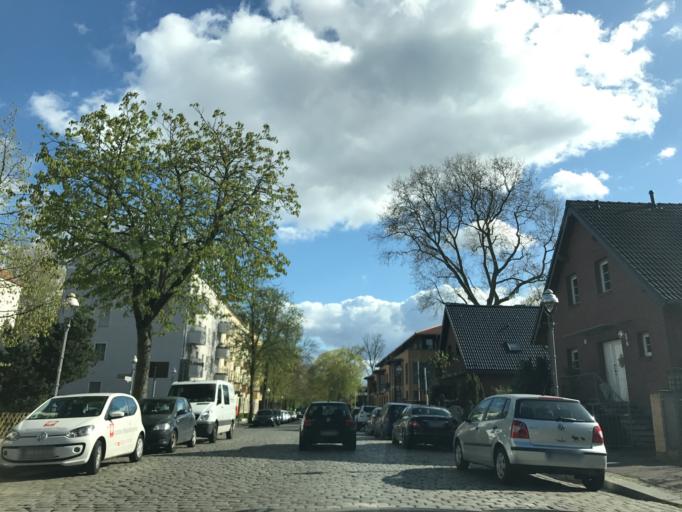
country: DE
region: Berlin
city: Tegel
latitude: 52.5870
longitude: 13.2764
